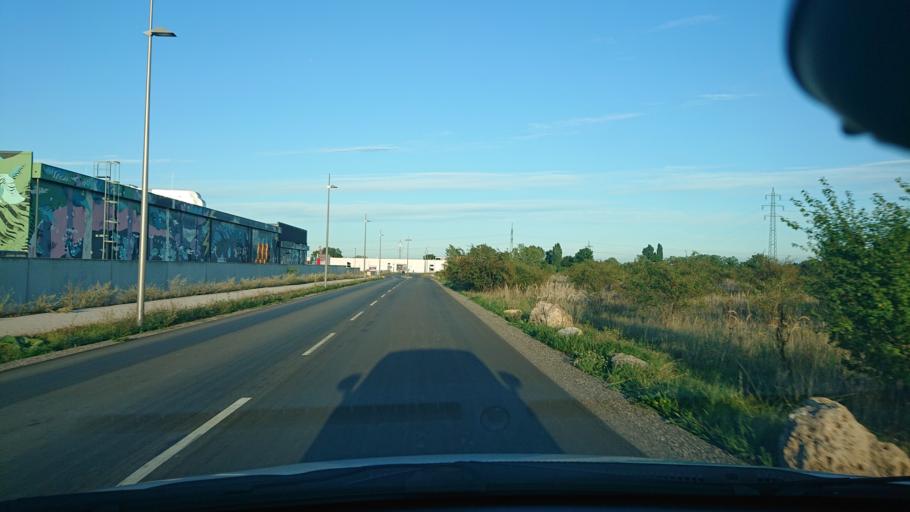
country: AT
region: Lower Austria
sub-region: Politischer Bezirk Baden
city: Leobersdorf
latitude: 47.9298
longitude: 16.1996
